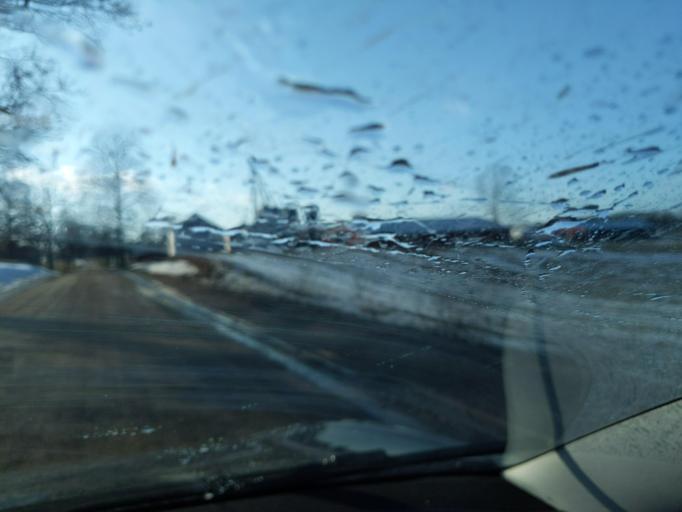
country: US
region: Michigan
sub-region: Ingham County
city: Stockbridge
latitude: 42.5173
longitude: -84.1492
